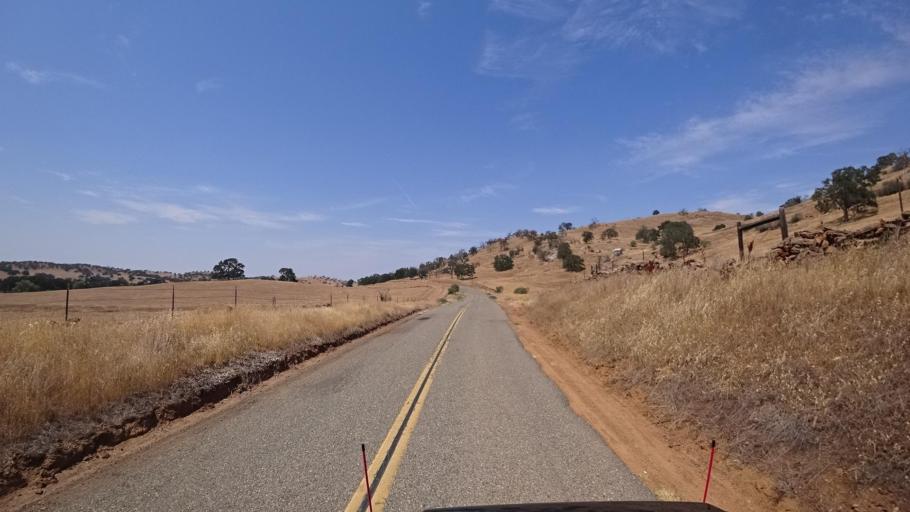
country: US
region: California
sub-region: Merced County
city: Planada
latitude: 37.5108
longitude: -120.2392
